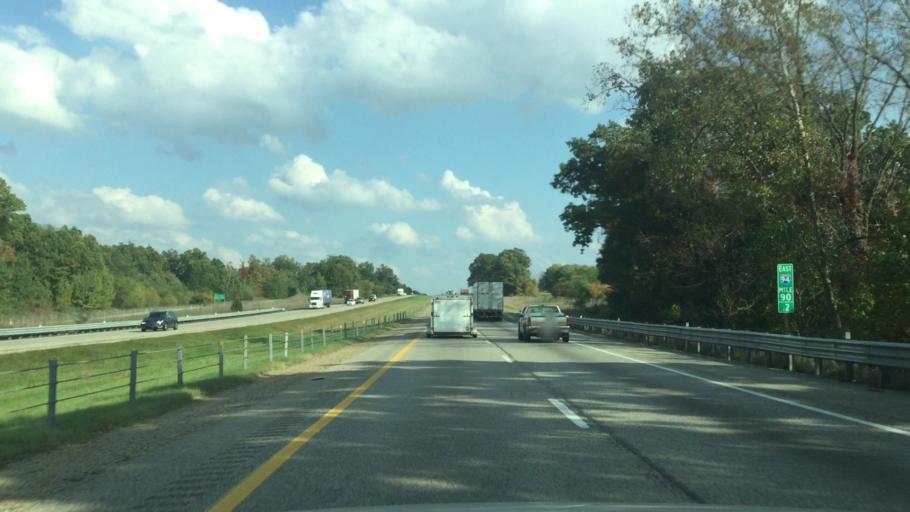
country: US
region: Michigan
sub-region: Kalamazoo County
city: Galesburg
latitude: 42.2792
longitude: -85.3316
